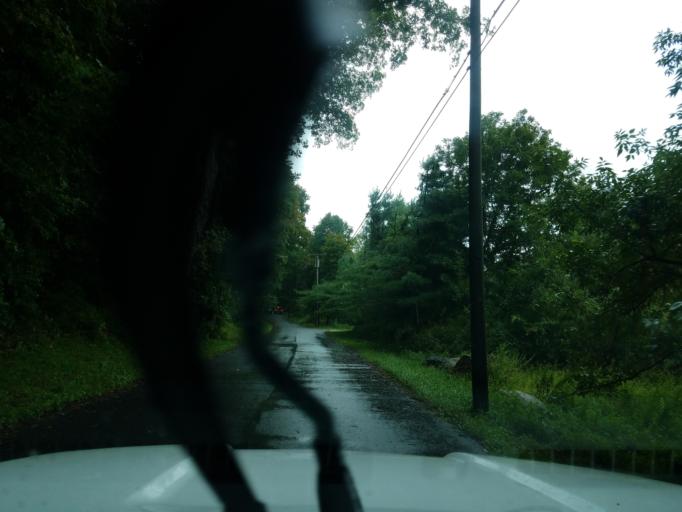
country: US
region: Connecticut
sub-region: Litchfield County
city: Kent
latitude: 41.7205
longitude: -73.4722
